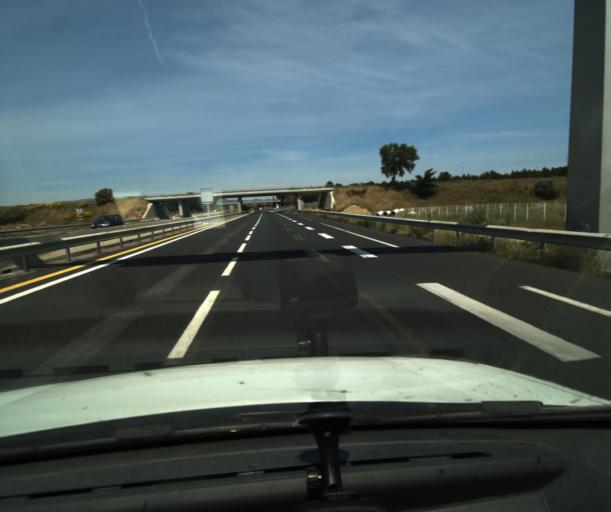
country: FR
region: Languedoc-Roussillon
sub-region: Departement des Pyrenees-Orientales
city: Rivesaltes
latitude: 42.7804
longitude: 2.8948
